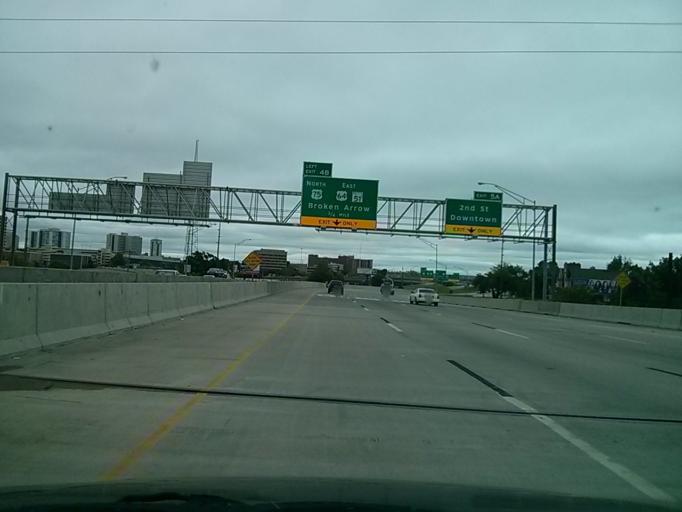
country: US
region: Oklahoma
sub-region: Tulsa County
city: Tulsa
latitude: 36.1564
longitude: -96.0017
